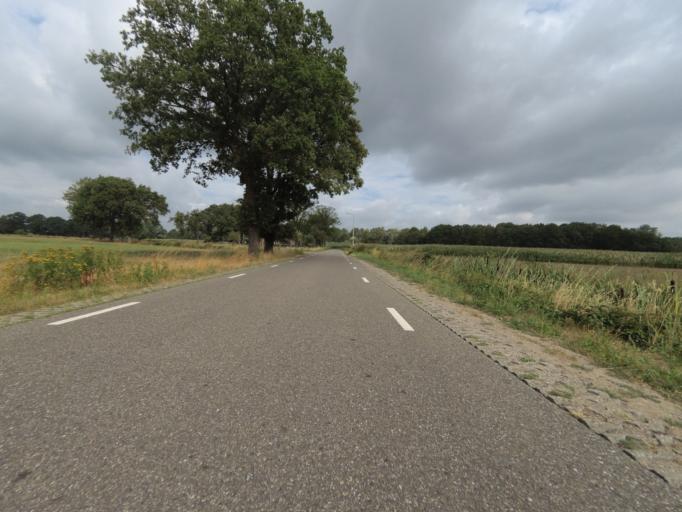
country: NL
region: Overijssel
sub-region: Gemeente Hengelo
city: Hengelo
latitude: 52.3116
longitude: 6.8341
